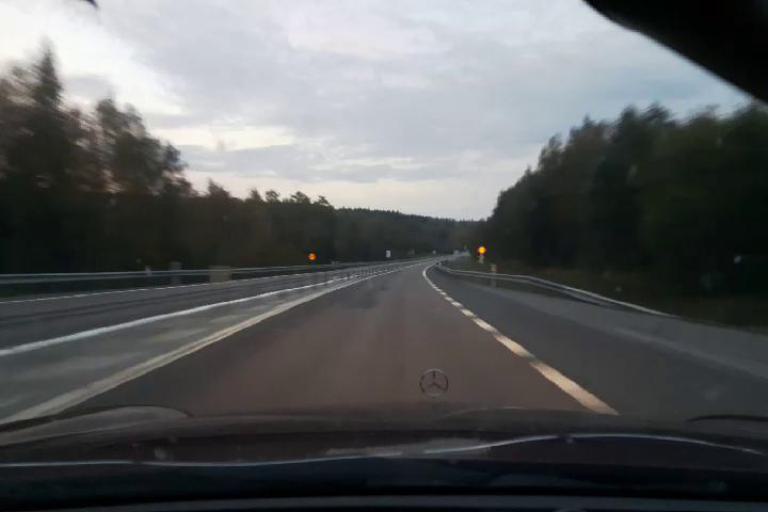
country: SE
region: Vaesternorrland
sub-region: Kramfors Kommun
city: Nordingra
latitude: 62.9534
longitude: 18.0986
